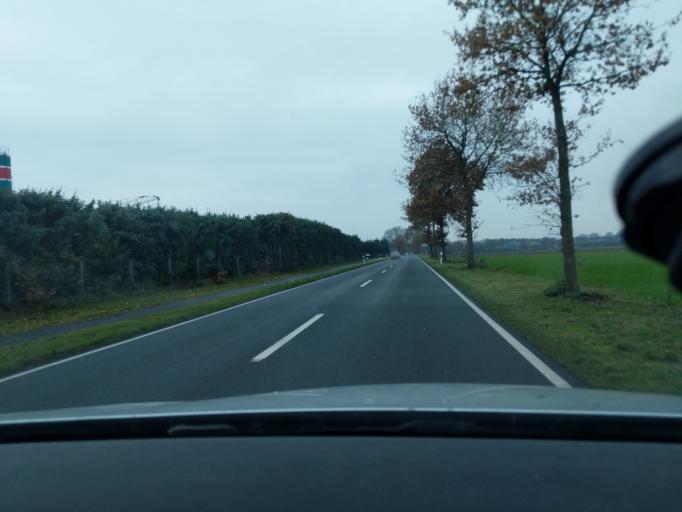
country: DE
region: Lower Saxony
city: Heeslingen
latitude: 53.3273
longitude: 9.3547
